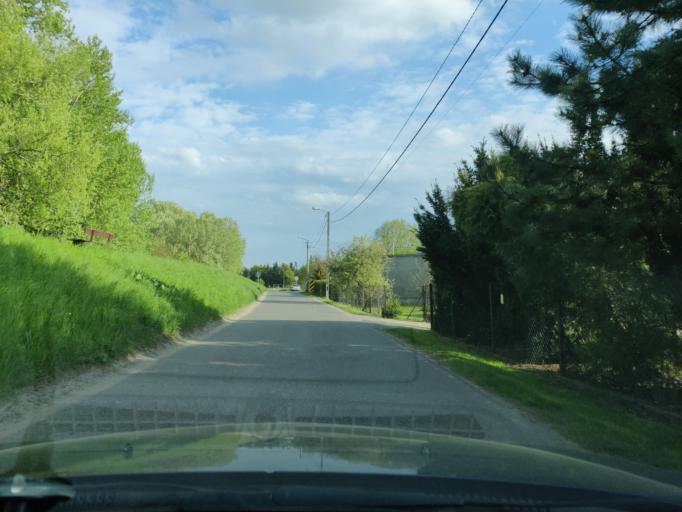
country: PL
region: Masovian Voivodeship
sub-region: Powiat otwocki
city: Jozefow
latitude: 52.1142
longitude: 21.1823
